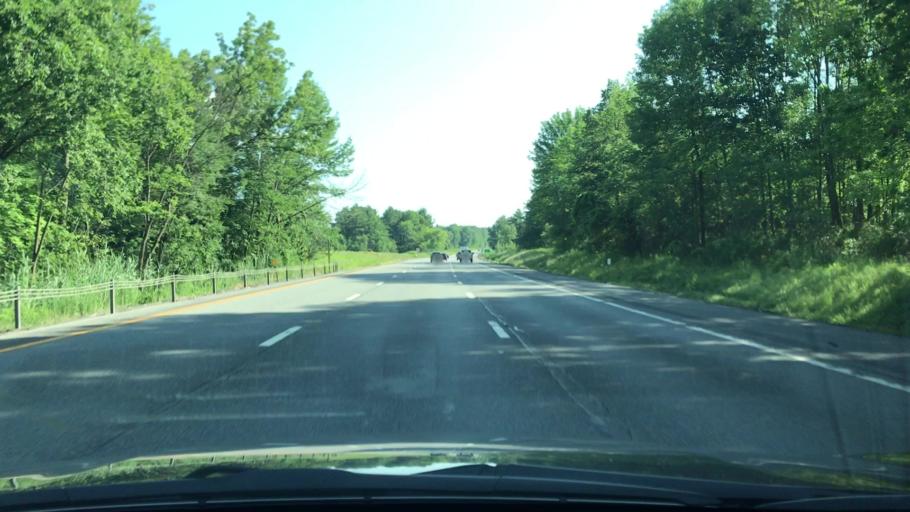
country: US
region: New York
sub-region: Warren County
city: West Glens Falls
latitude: 43.2072
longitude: -73.6953
